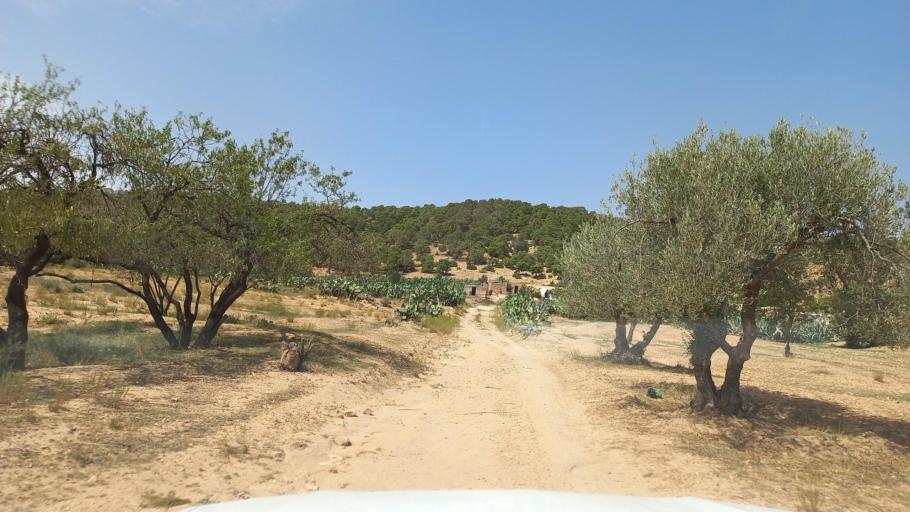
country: TN
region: Al Qasrayn
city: Kasserine
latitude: 35.3781
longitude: 8.9096
